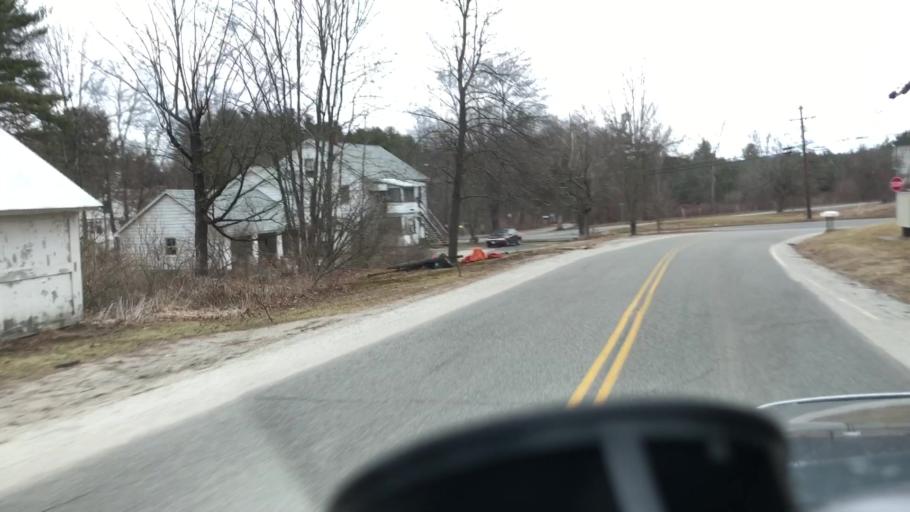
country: US
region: Massachusetts
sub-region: Hampshire County
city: Southampton
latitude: 42.2152
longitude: -72.7308
